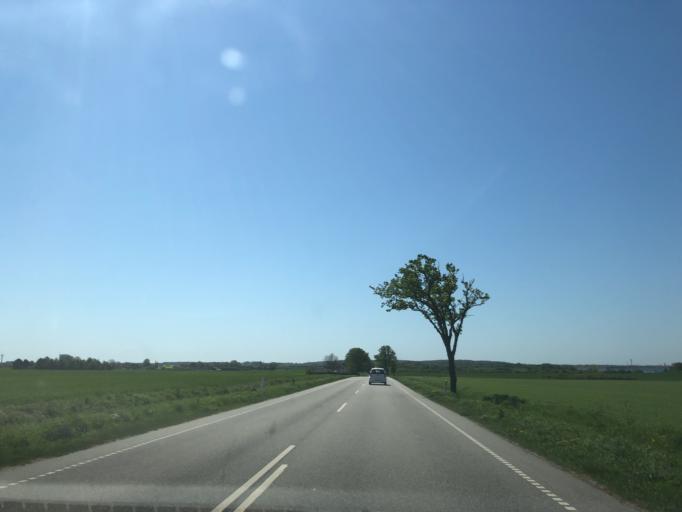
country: DK
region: Zealand
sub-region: Slagelse Kommune
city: Forlev
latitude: 55.3432
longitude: 11.2256
